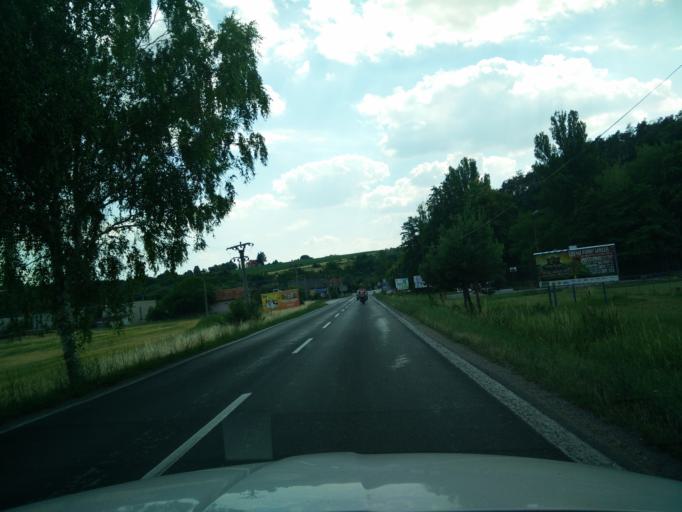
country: SK
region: Nitriansky
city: Partizanske
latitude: 48.6907
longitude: 18.3786
